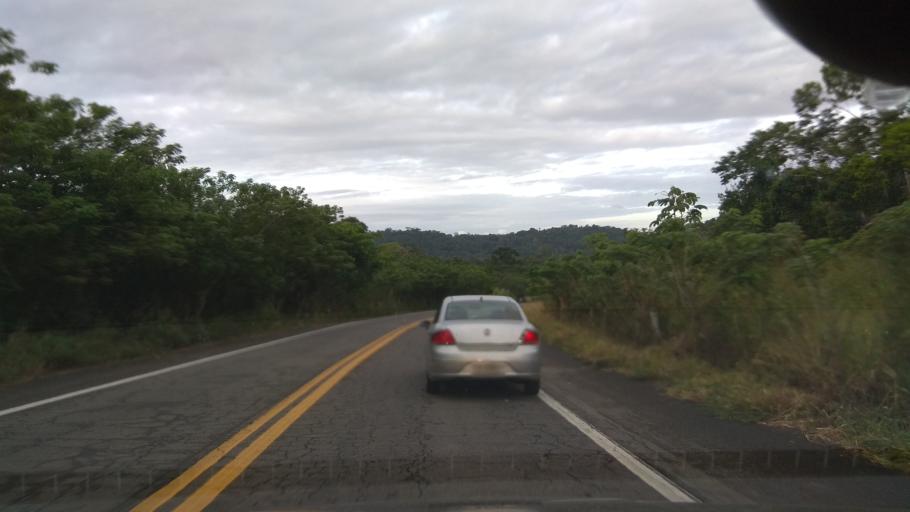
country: BR
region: Bahia
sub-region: Ubaitaba
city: Ubaitaba
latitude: -14.2621
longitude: -39.3342
